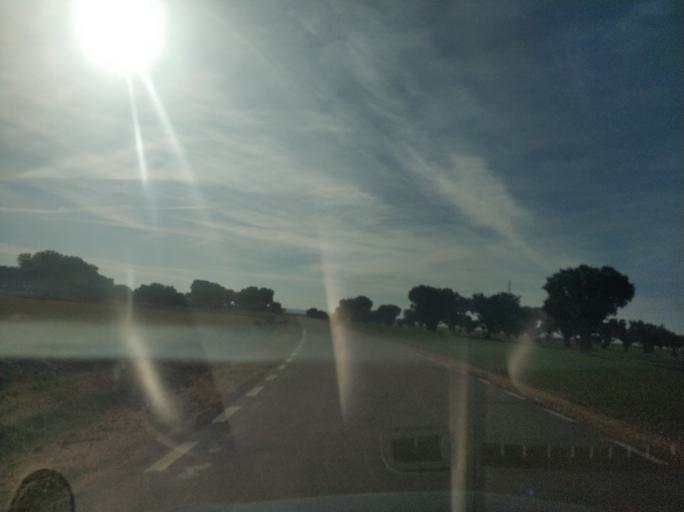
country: ES
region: Castille and Leon
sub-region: Provincia de Salamanca
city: Parada de Arriba
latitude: 40.9997
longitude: -5.8133
